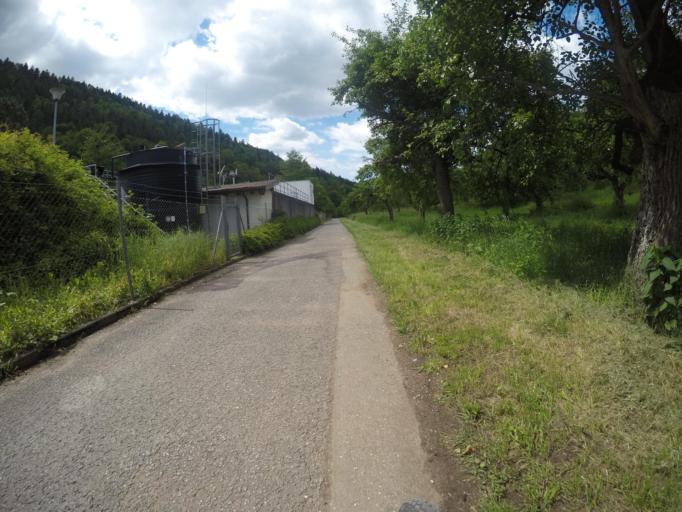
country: DE
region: Baden-Wuerttemberg
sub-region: Karlsruhe Region
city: Unterreichenbach
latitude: 48.8326
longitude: 8.7031
